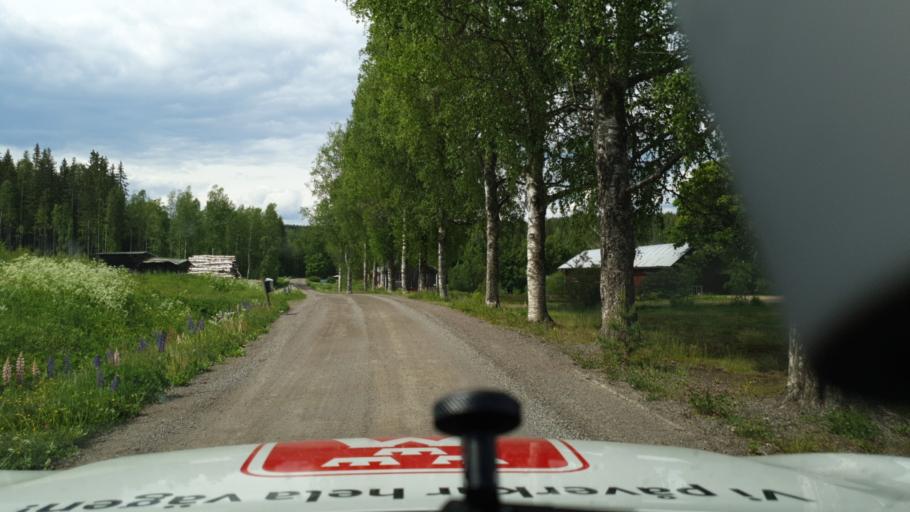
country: SE
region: Vaermland
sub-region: Torsby Kommun
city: Torsby
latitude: 59.9815
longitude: 12.8381
